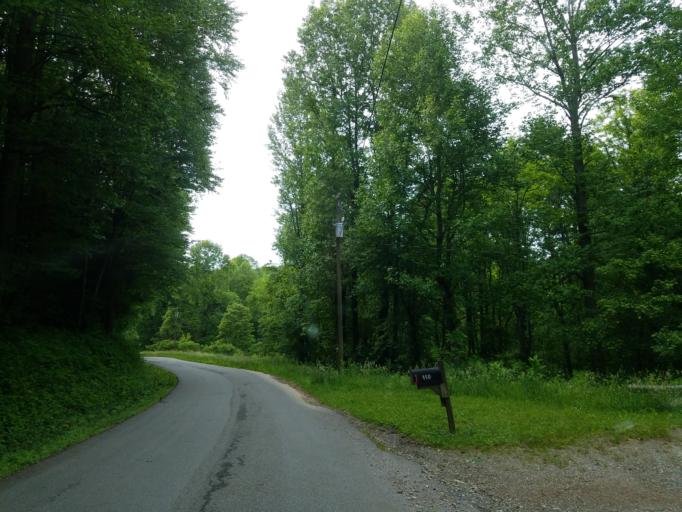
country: US
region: Georgia
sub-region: Union County
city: Blairsville
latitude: 34.7379
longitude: -83.9822
